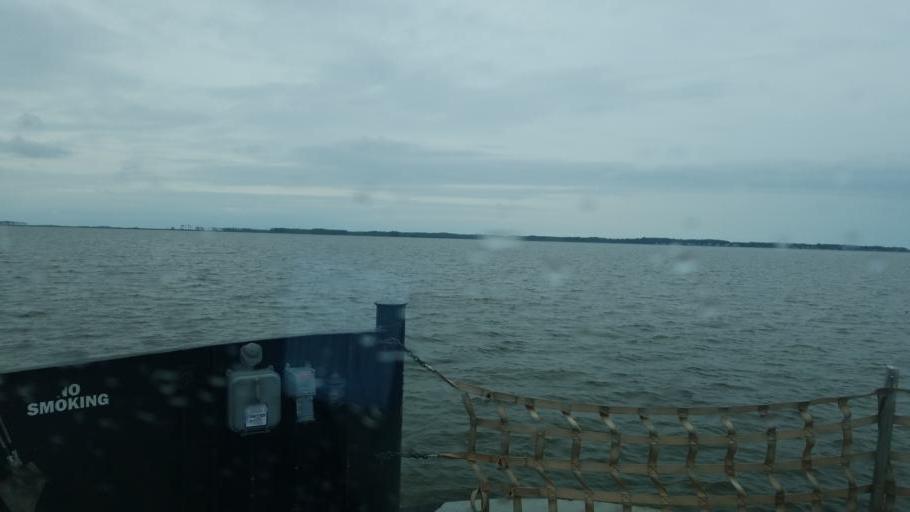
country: US
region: North Carolina
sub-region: Currituck County
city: Currituck
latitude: 36.4680
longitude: -75.9592
